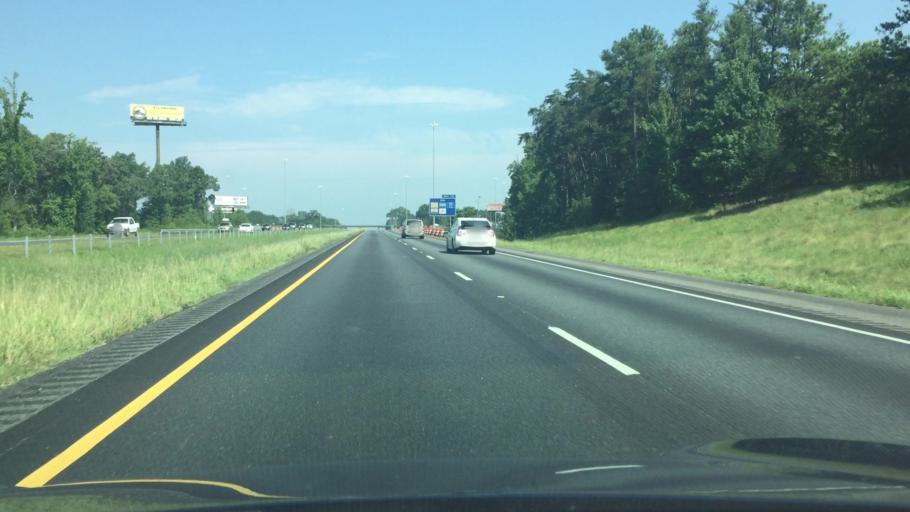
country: US
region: Alabama
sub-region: Chilton County
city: Jemison
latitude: 32.9732
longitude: -86.6835
